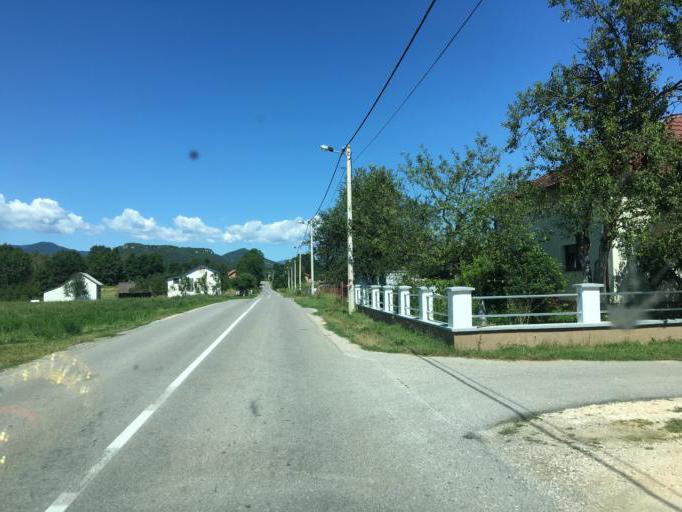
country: HR
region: Licko-Senjska
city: Gospic
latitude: 44.5606
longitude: 15.3287
